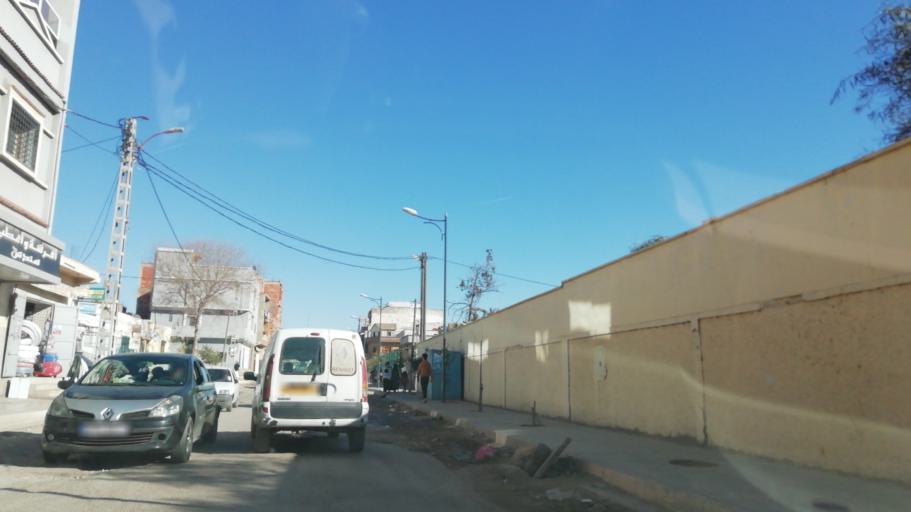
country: DZ
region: Oran
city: Bir el Djir
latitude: 35.7257
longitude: -0.5403
